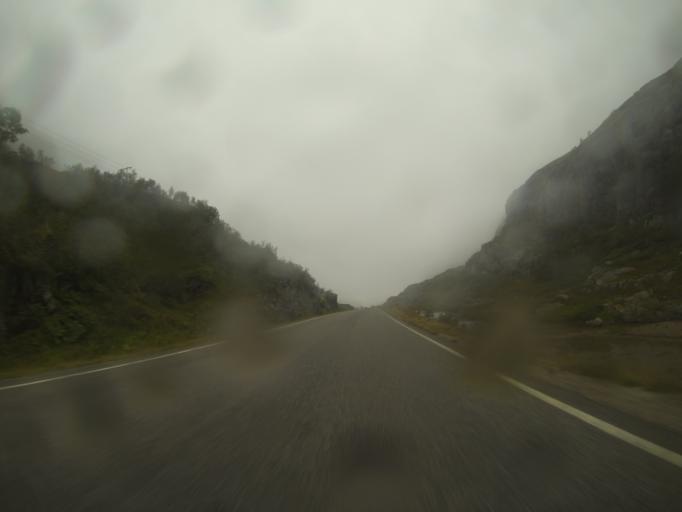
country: NO
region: Vest-Agder
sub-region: Sirdal
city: Tonstad
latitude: 58.8984
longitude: 6.6813
